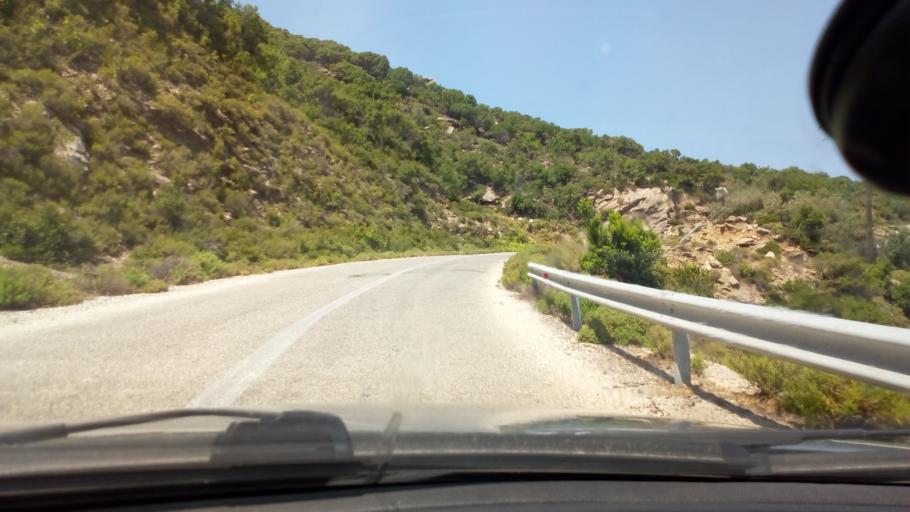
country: GR
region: North Aegean
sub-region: Nomos Samou
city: Agios Kirykos
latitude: 37.6377
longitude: 26.2549
